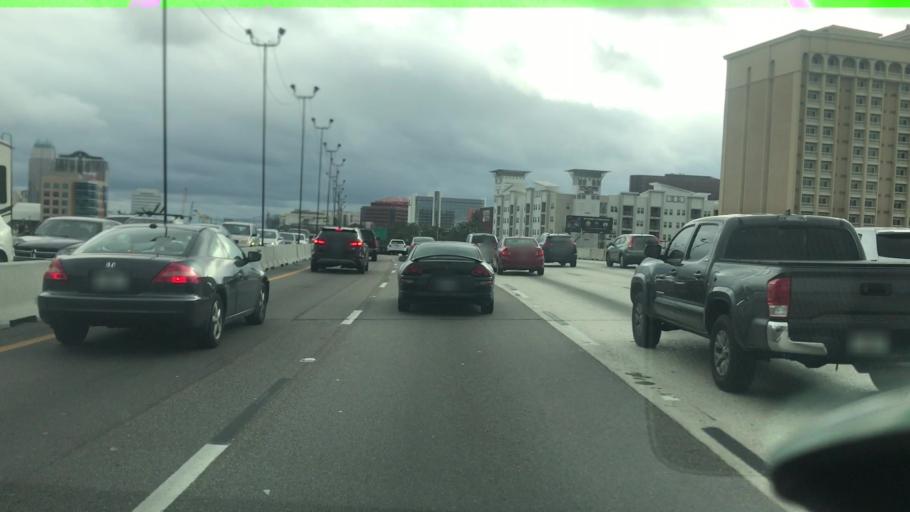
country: US
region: Florida
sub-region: Orange County
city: Orlando
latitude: 28.5532
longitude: -81.3825
